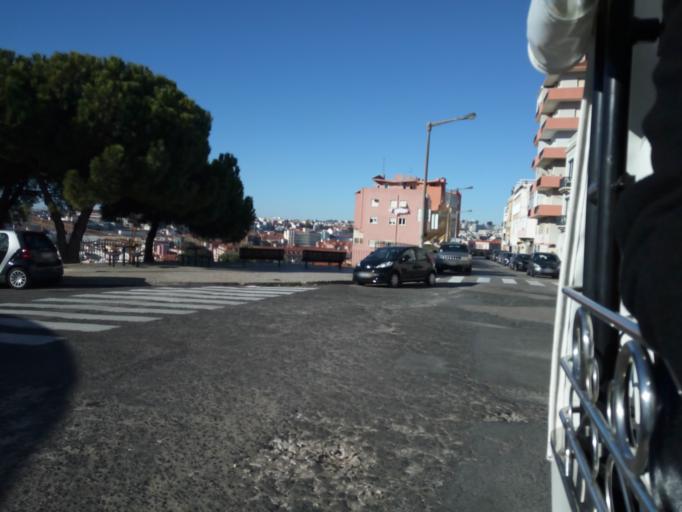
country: PT
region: Lisbon
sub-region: Lisbon
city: Lisbon
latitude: 38.7182
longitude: -9.1312
